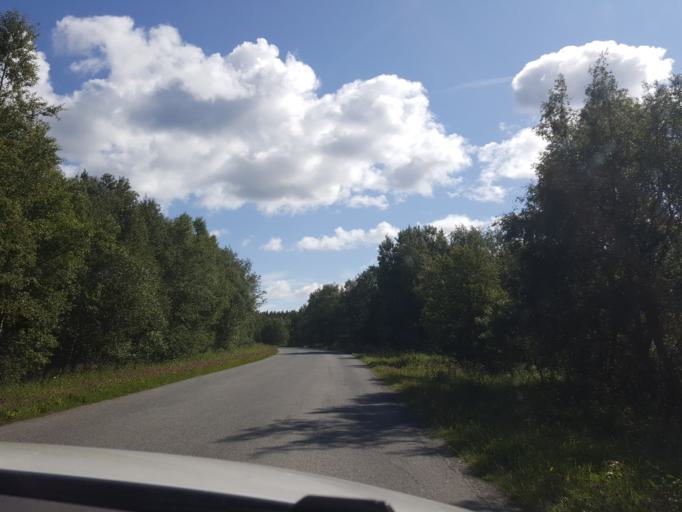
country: NO
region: Nordland
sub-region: Bodo
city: Loding
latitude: 67.2309
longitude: 14.9181
